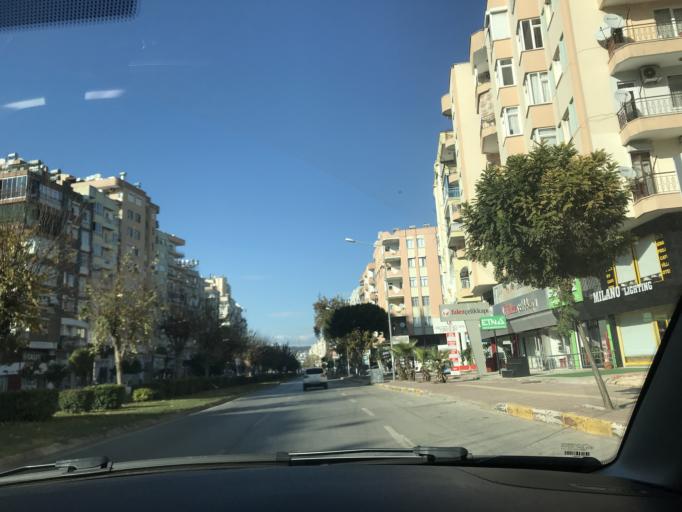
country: TR
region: Antalya
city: Antalya
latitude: 36.9043
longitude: 30.7008
